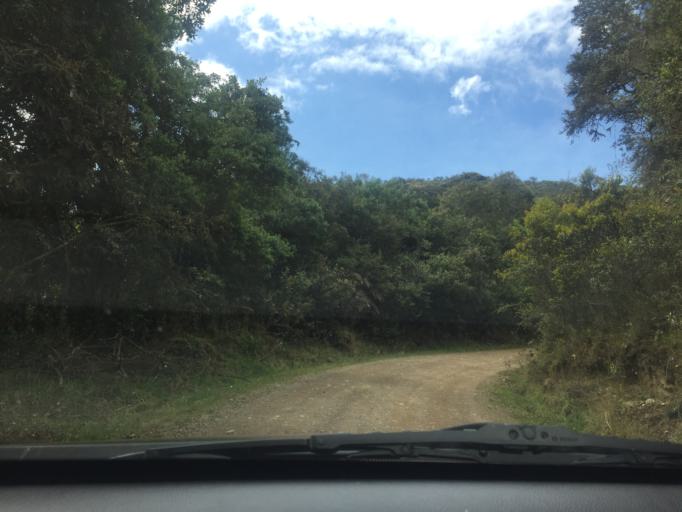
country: CO
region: Cundinamarca
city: Facatativa
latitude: 4.7925
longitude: -74.3807
